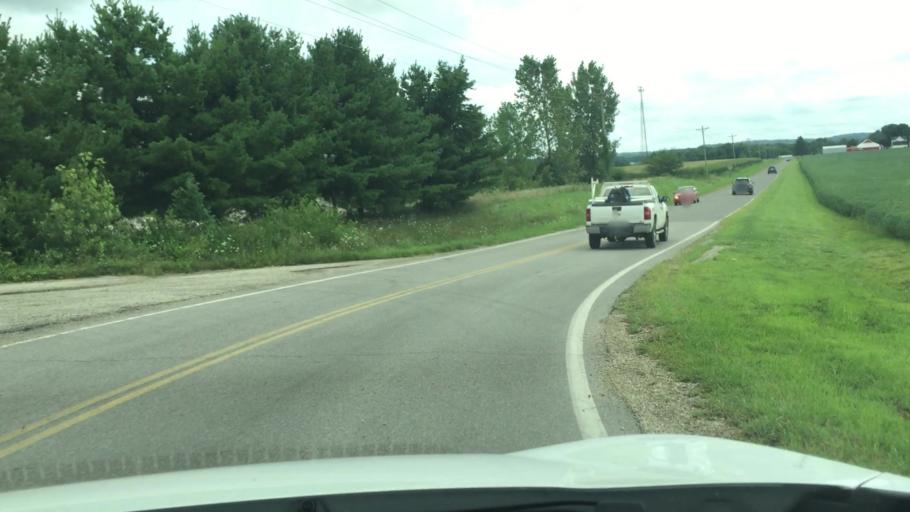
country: US
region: Ohio
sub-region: Champaign County
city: Mechanicsburg
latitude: 40.0396
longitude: -83.6560
